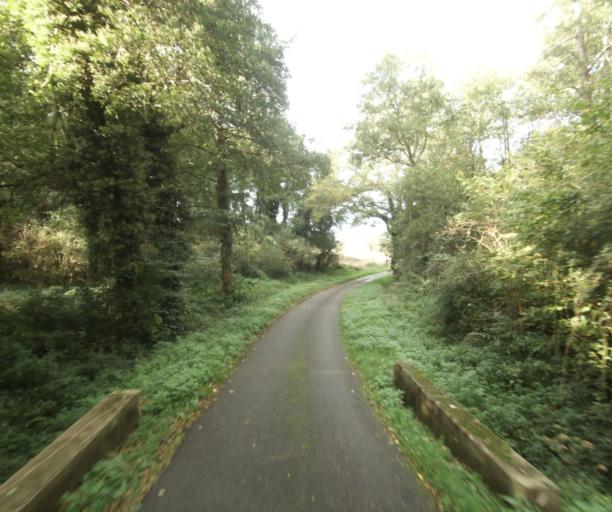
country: FR
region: Midi-Pyrenees
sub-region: Departement du Gers
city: Le Houga
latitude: 43.8571
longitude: -0.1562
